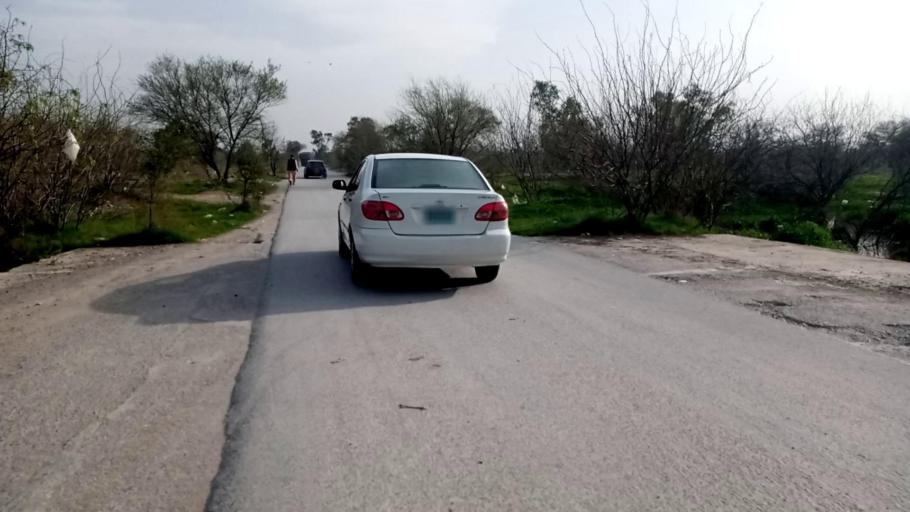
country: PK
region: Khyber Pakhtunkhwa
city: Peshawar
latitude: 34.0053
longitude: 71.4520
